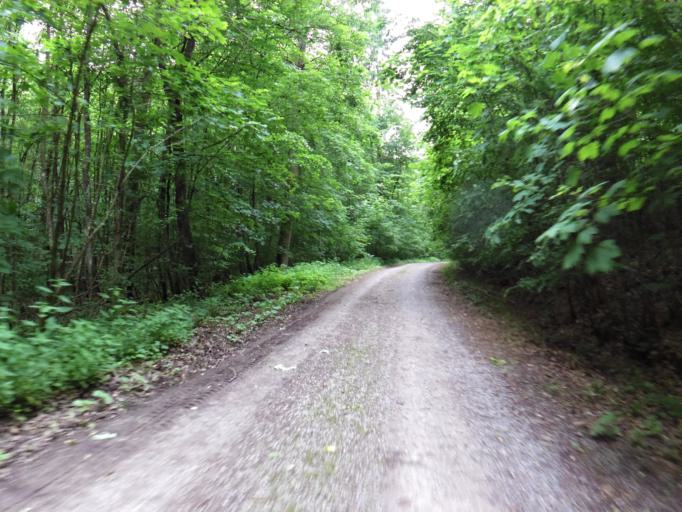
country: DE
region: Bavaria
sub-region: Regierungsbezirk Unterfranken
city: Margetshochheim
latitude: 49.8208
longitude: 9.8431
